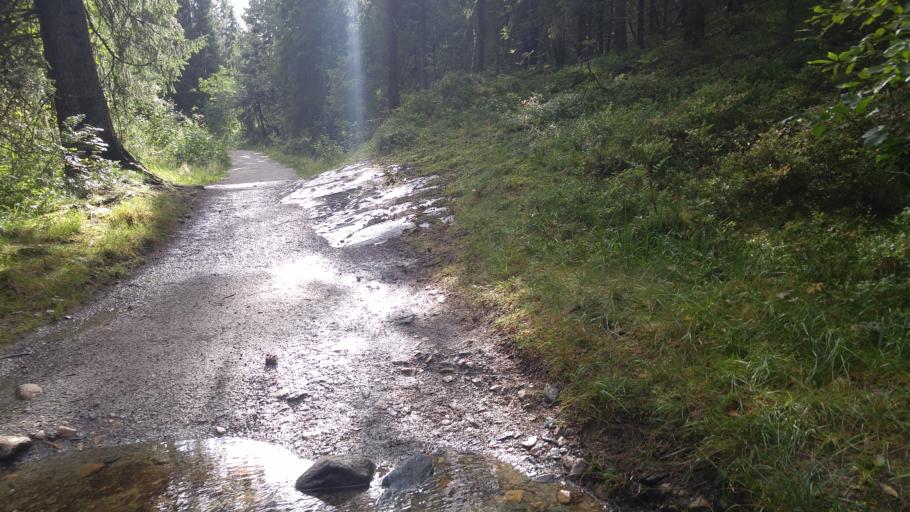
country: NO
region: Sor-Trondelag
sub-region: Trondheim
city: Trondheim
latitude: 63.4074
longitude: 10.3222
